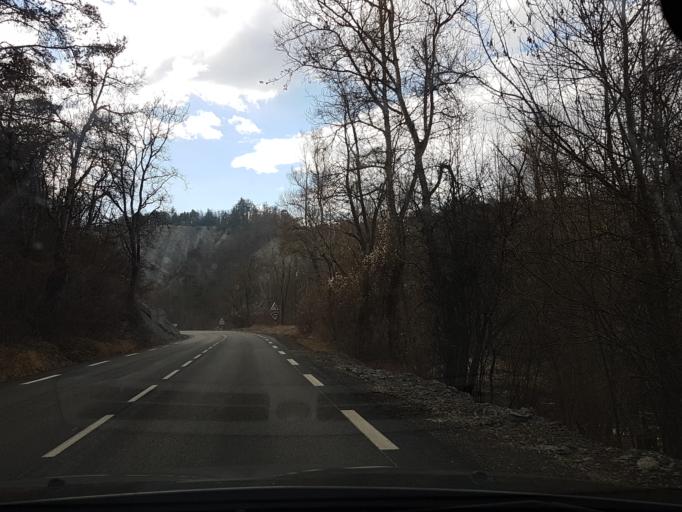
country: FR
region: Provence-Alpes-Cote d'Azur
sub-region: Departement des Hautes-Alpes
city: Tallard
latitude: 44.5125
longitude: 6.0646
